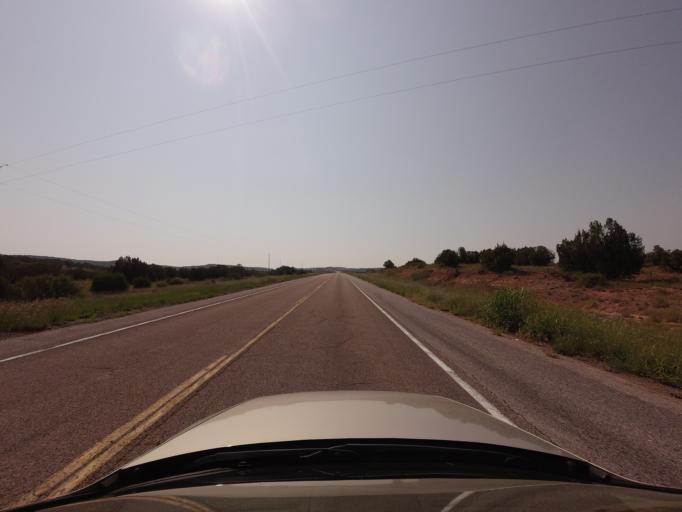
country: US
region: New Mexico
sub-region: Quay County
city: Tucumcari
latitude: 34.8343
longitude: -103.7567
